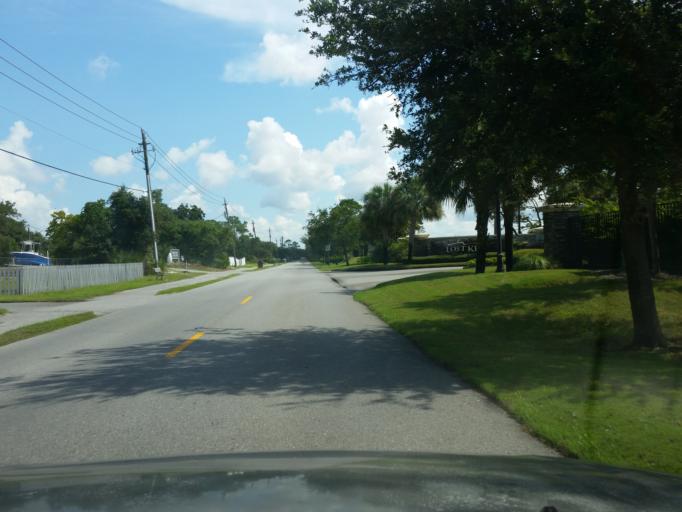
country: US
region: Alabama
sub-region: Baldwin County
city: Orange Beach
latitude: 30.3066
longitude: -87.4402
